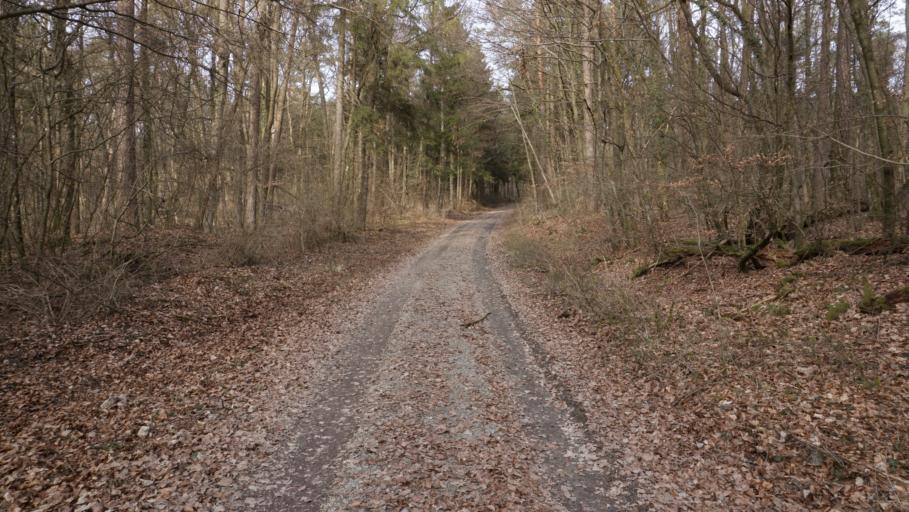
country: DE
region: Baden-Wuerttemberg
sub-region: Karlsruhe Region
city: Mosbach
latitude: 49.3867
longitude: 9.1685
